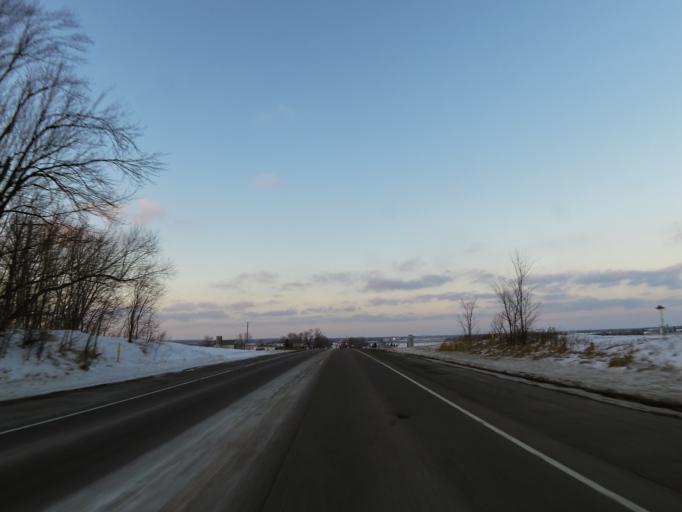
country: US
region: Minnesota
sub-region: Dakota County
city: Farmington
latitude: 44.6887
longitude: -93.1364
